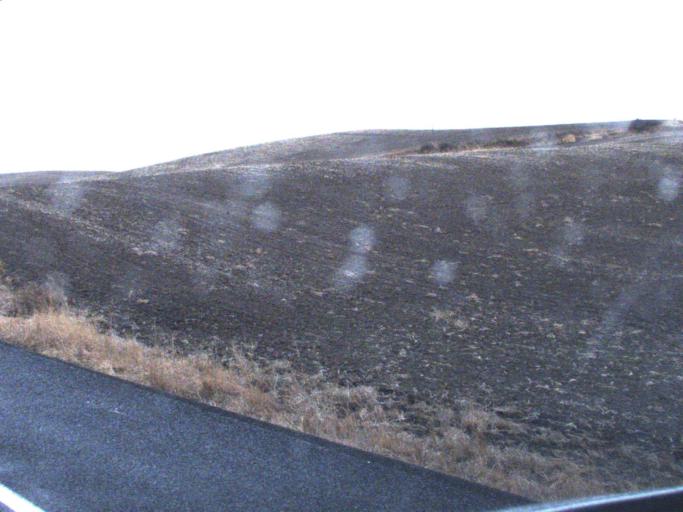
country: US
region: Washington
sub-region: Whitman County
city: Pullman
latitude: 46.6849
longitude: -117.1995
